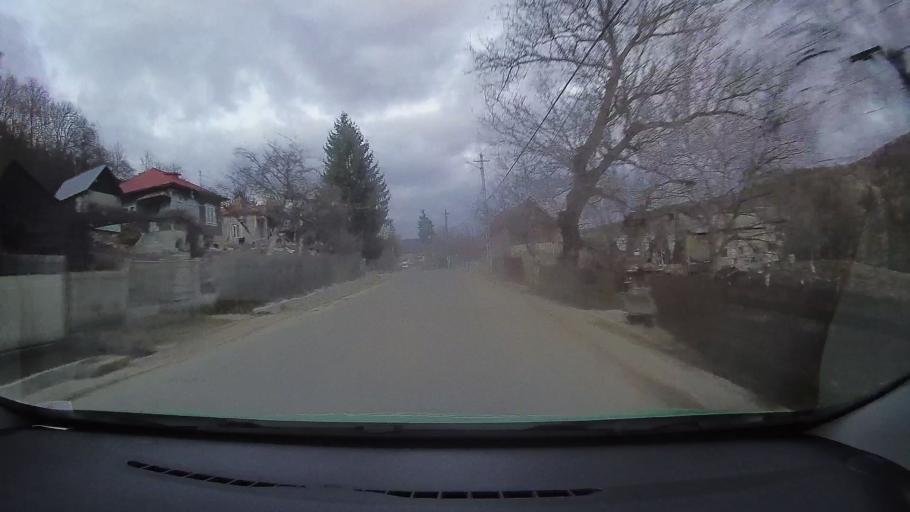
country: RO
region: Dambovita
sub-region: Comuna Visinesti
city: Visinesti
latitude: 45.1006
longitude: 25.5798
